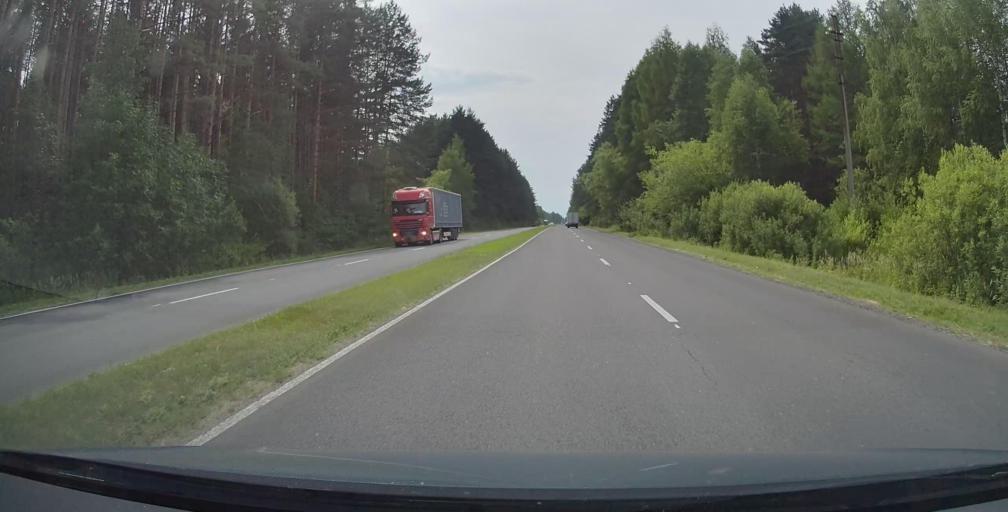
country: RU
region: Jaroslavl
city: Rybinsk
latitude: 58.0190
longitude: 38.9625
